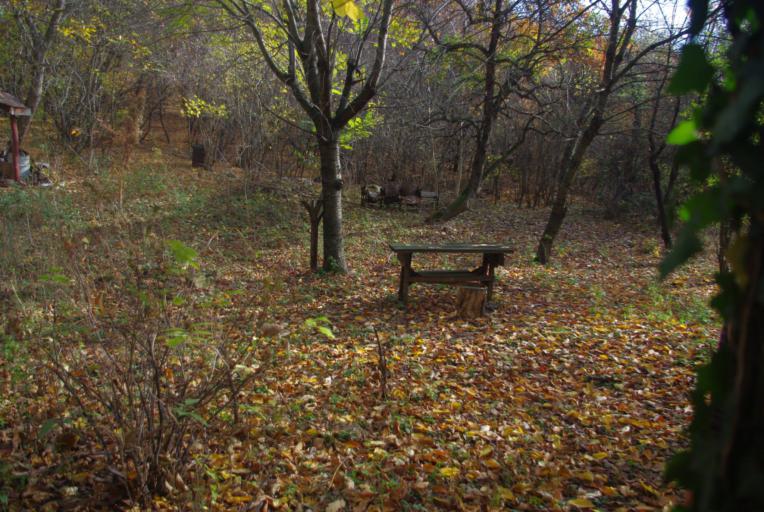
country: HU
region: Borsod-Abauj-Zemplen
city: Sarospatak
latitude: 48.3897
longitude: 21.5863
